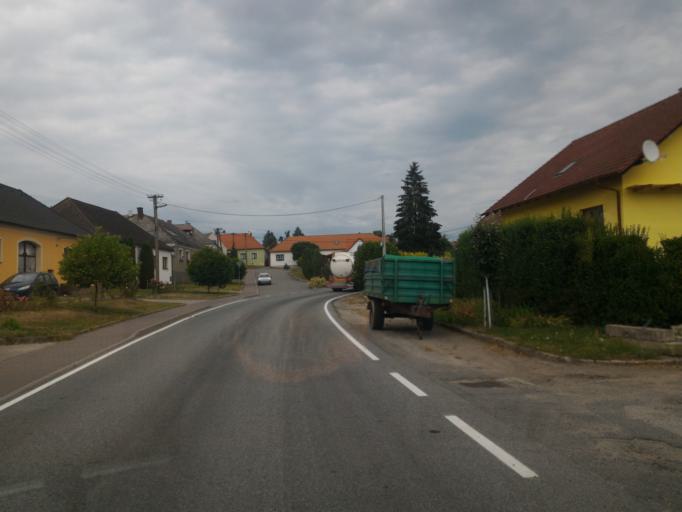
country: CZ
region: Vysocina
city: Zeletava
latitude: 49.1794
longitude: 15.5945
